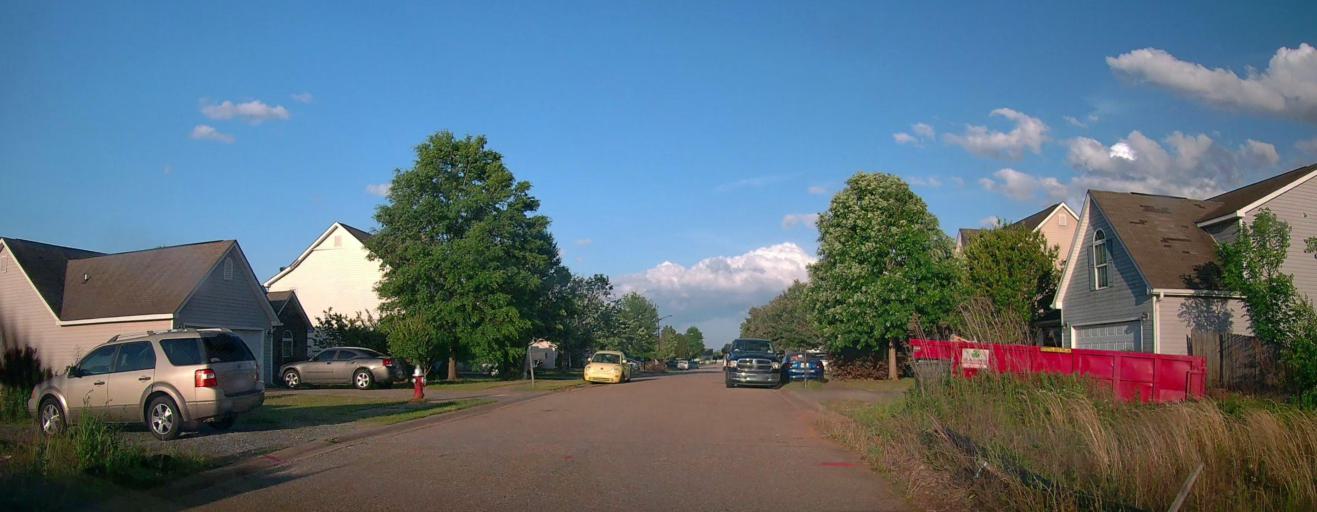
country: US
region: Georgia
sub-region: Houston County
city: Centerville
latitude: 32.6310
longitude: -83.7187
